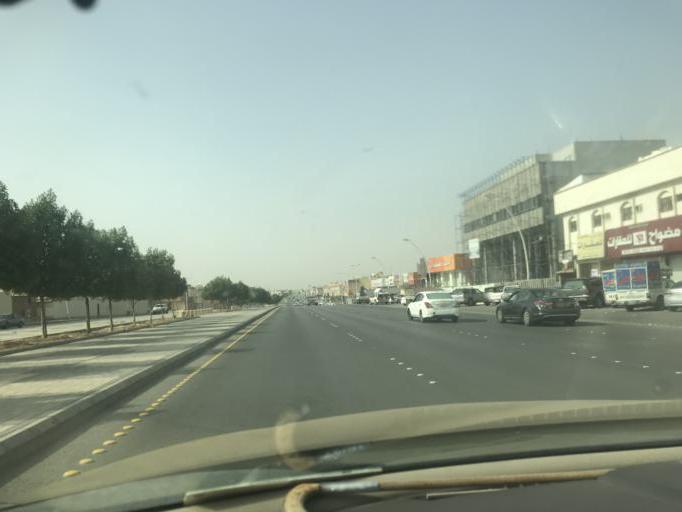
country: SA
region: Ar Riyad
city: Riyadh
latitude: 24.6751
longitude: 46.8023
